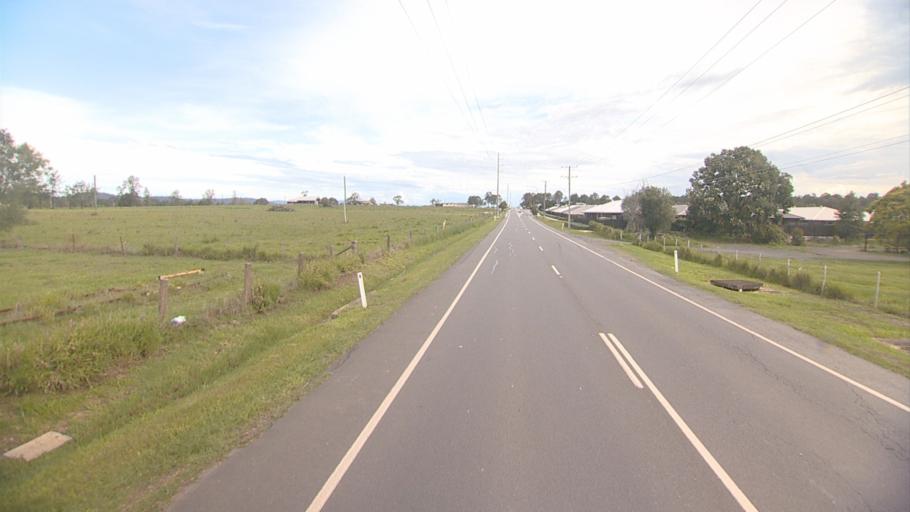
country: AU
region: Queensland
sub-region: Logan
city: Waterford West
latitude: -27.7083
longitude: 153.1167
